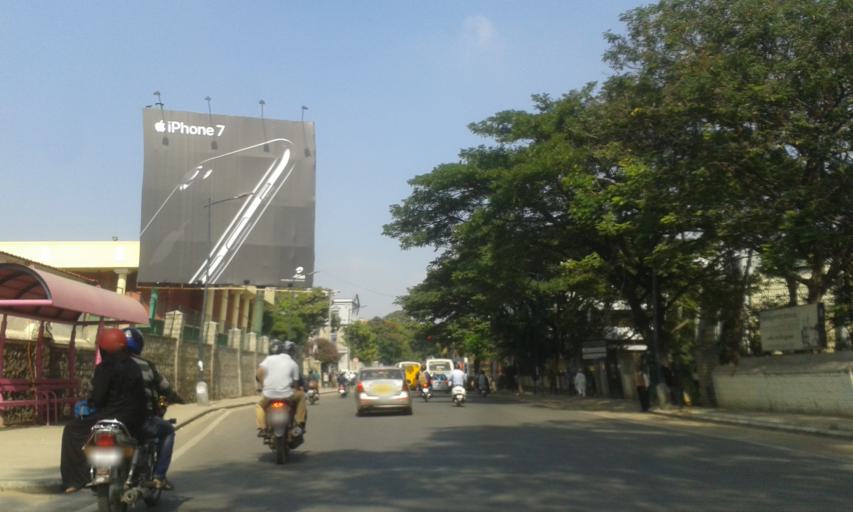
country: IN
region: Karnataka
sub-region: Bangalore Urban
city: Bangalore
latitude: 12.9698
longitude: 77.6053
